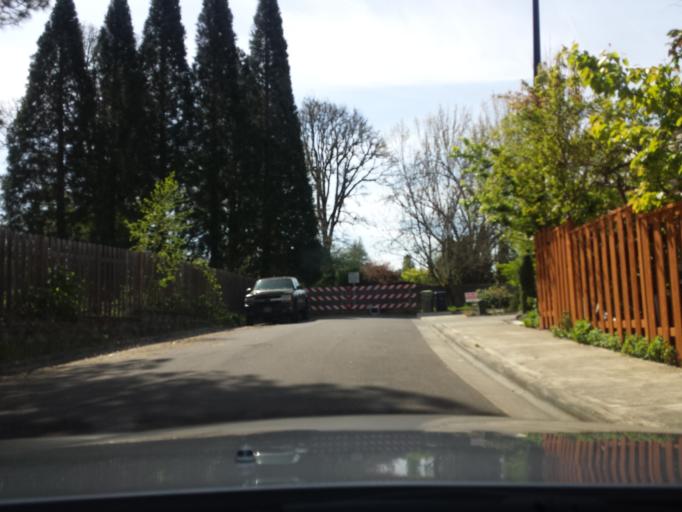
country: US
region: Oregon
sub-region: Washington County
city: Aloha
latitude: 45.4985
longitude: -122.8559
